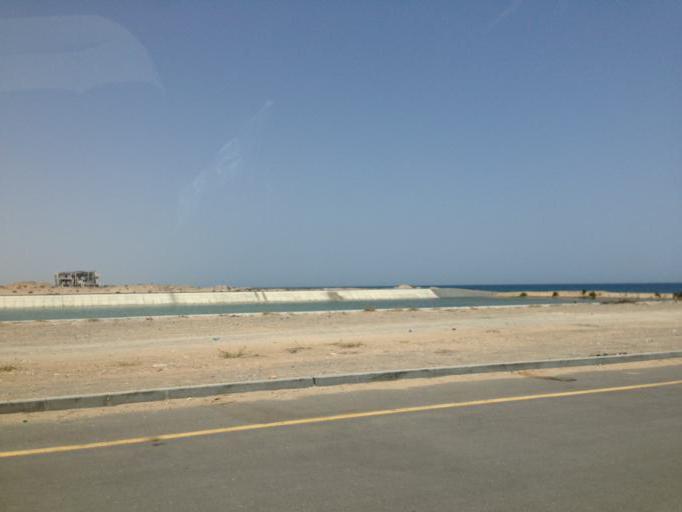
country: OM
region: Muhafazat Masqat
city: Bawshar
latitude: 23.6074
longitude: 58.3216
